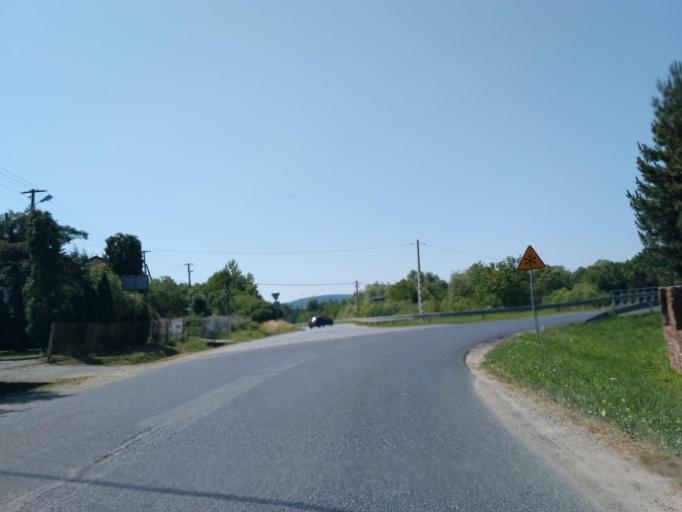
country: PL
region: Subcarpathian Voivodeship
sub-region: Powiat sanocki
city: Niebieszczany
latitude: 49.5382
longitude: 22.1300
